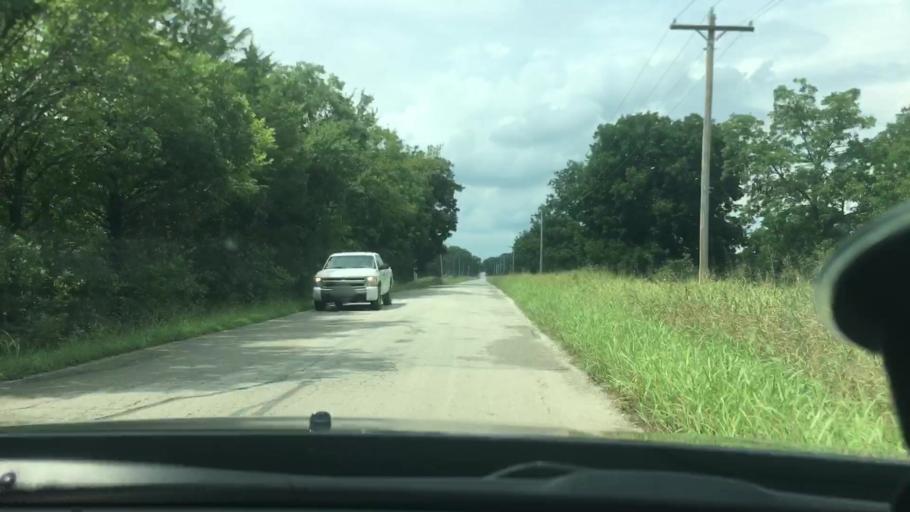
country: US
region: Oklahoma
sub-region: Carter County
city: Dickson
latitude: 34.2527
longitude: -96.9431
